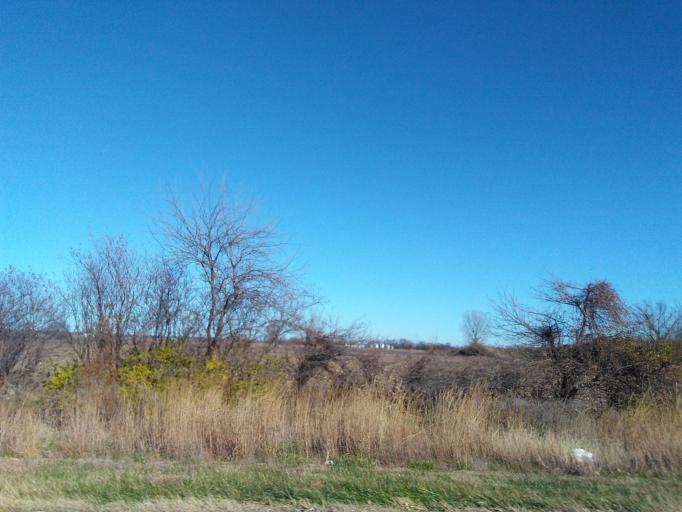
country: US
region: Illinois
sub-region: Saint Clair County
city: Dupo
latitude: 38.4788
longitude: -90.2483
